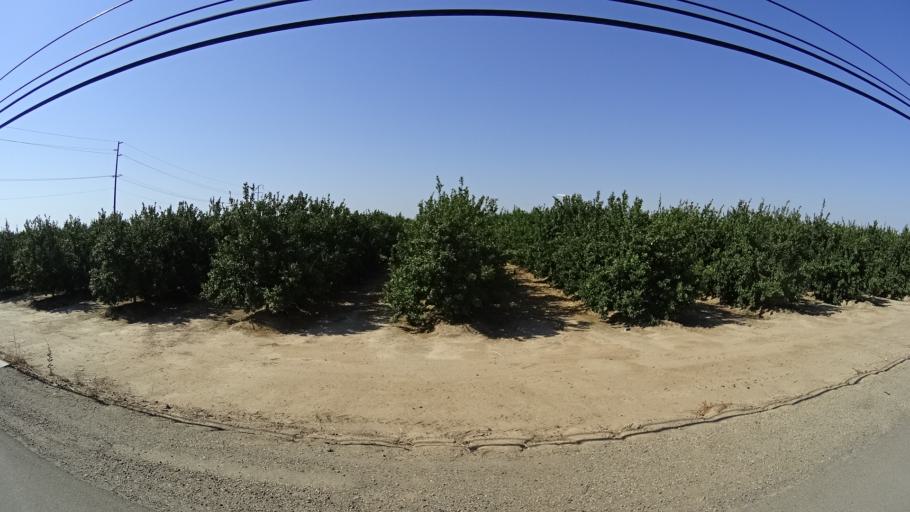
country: US
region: California
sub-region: Fresno County
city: Sunnyside
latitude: 36.7074
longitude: -119.6919
